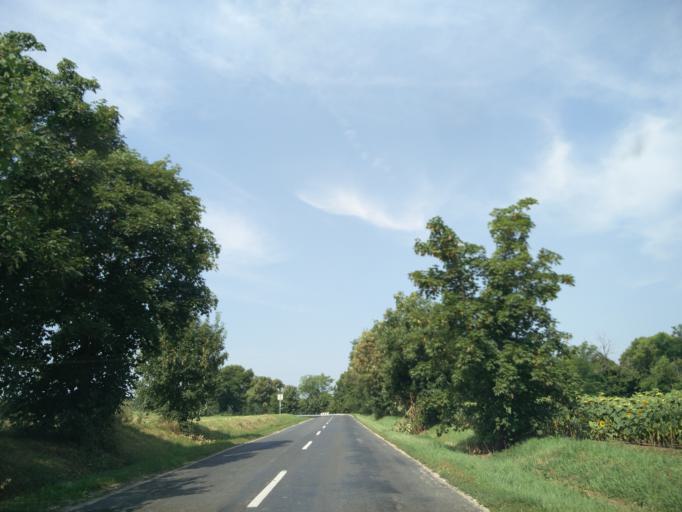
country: HU
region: Fejer
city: Bicske
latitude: 47.4347
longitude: 18.6417
